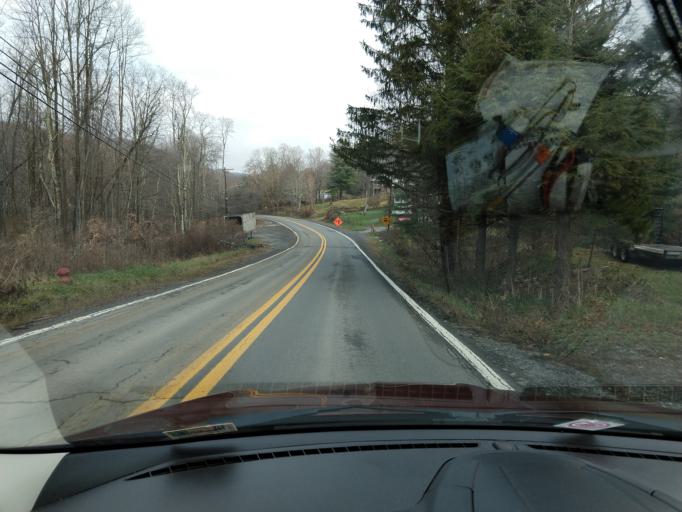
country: US
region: West Virginia
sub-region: Greenbrier County
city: Rainelle
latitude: 38.0615
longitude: -80.7080
